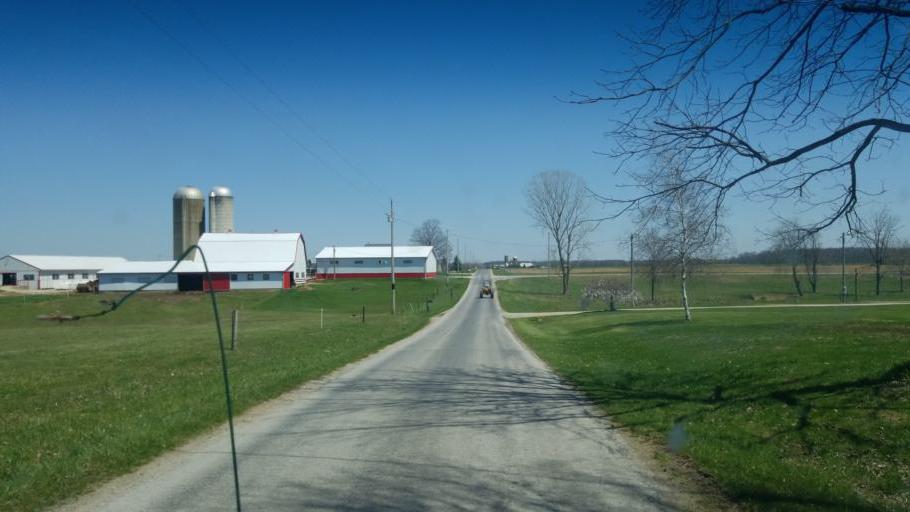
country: US
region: Ohio
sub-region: Huron County
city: Greenwich
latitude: 41.0471
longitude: -82.4621
